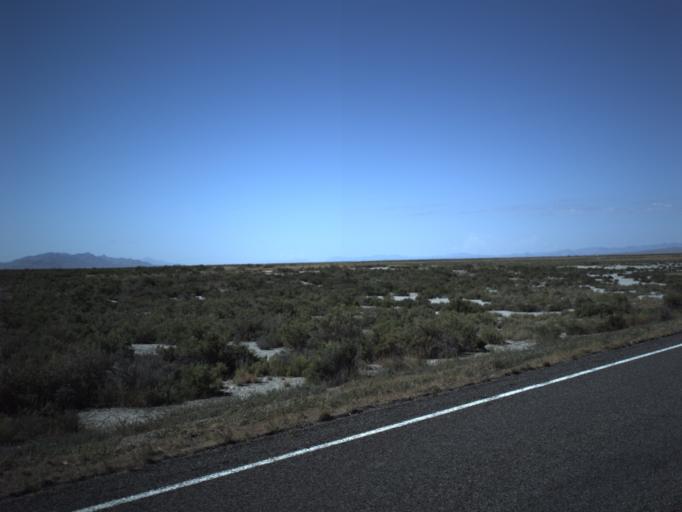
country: US
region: Utah
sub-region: Millard County
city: Delta
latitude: 39.3071
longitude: -112.7918
